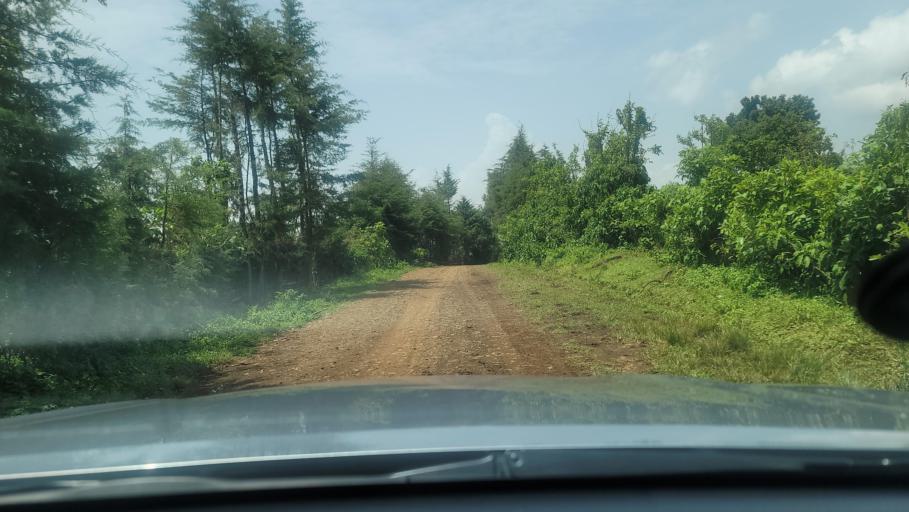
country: ET
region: Oromiya
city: Agaro
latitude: 7.8332
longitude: 36.4057
